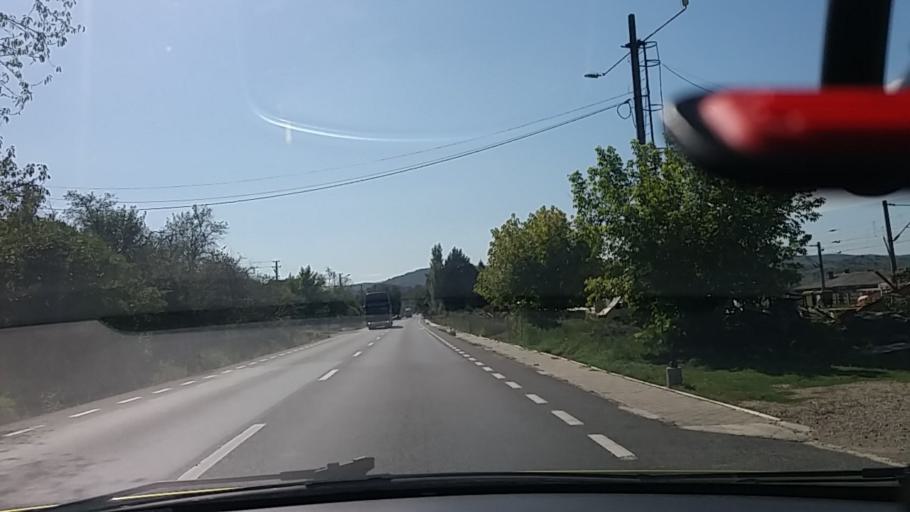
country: RO
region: Hunedoara
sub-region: Comuna Zam
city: Zam
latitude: 46.0030
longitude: 22.4418
